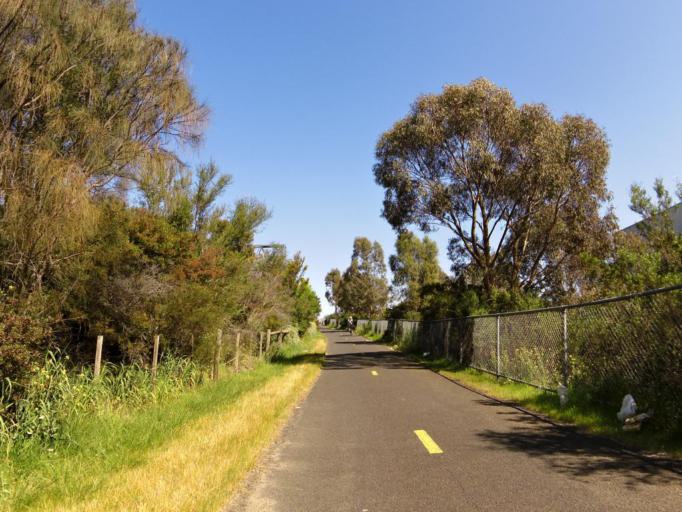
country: AU
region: Victoria
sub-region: Whittlesea
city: Thomastown
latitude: -37.6856
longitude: 145.0148
